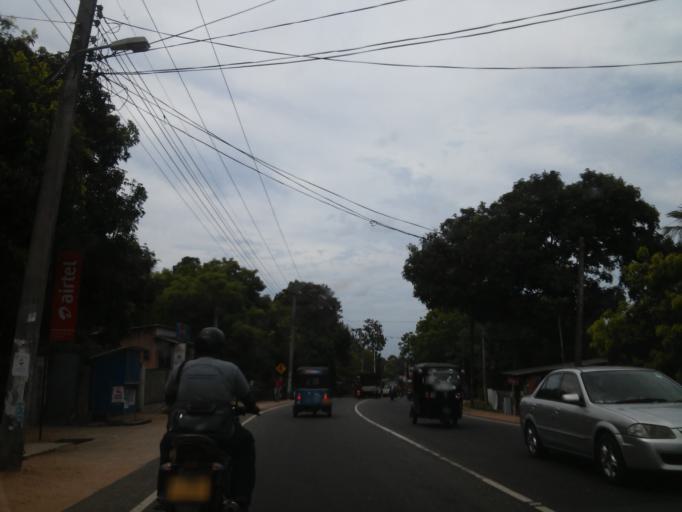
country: LK
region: Eastern Province
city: Trincomalee
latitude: 8.5870
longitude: 81.2127
